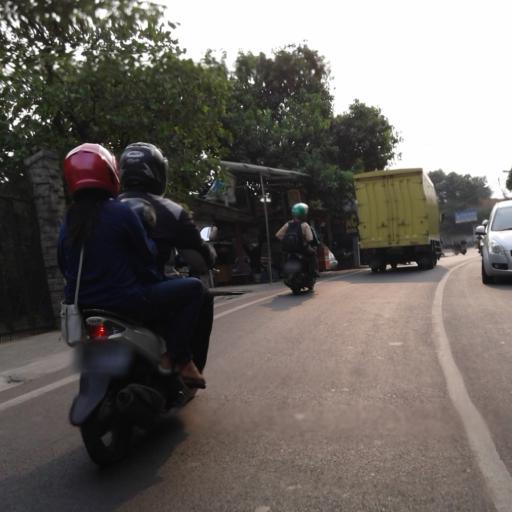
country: ID
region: West Java
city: Sawangan
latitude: -6.4036
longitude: 106.7670
